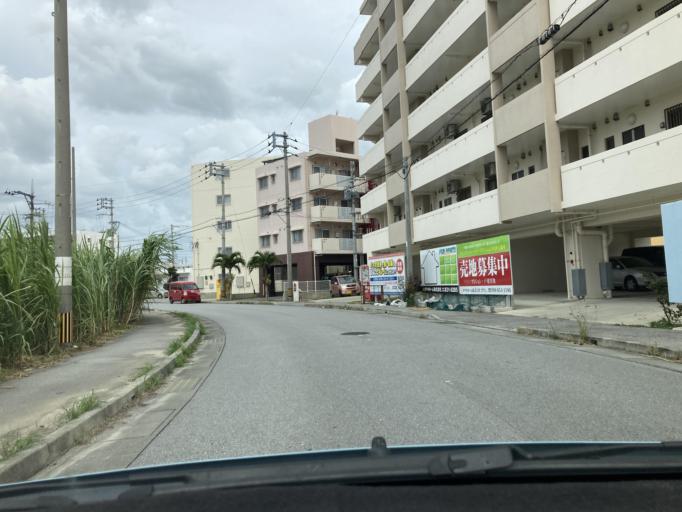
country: JP
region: Okinawa
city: Ginowan
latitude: 26.1858
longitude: 127.7773
